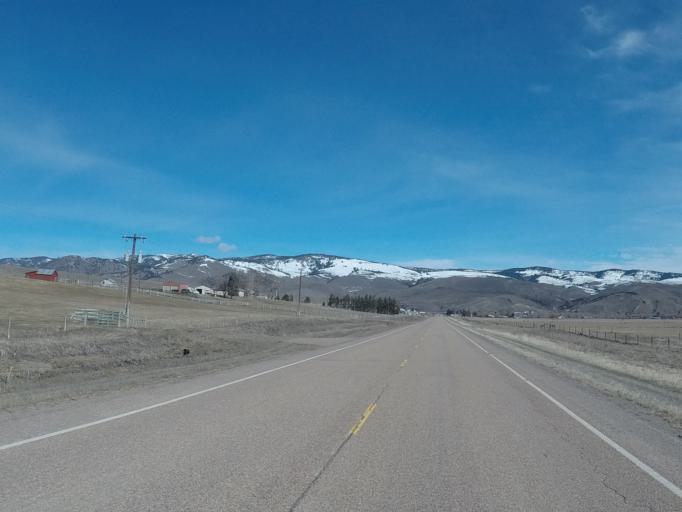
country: US
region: Montana
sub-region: Granite County
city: Philipsburg
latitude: 46.6469
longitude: -113.1636
